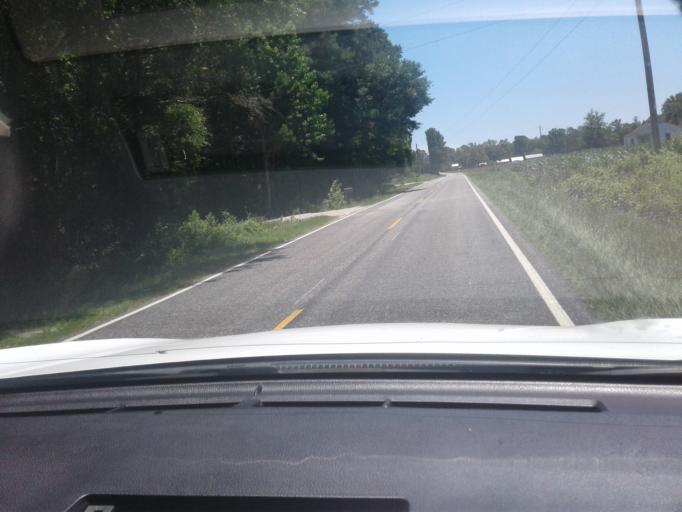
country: US
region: North Carolina
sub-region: Harnett County
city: Lillington
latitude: 35.3446
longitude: -78.9065
